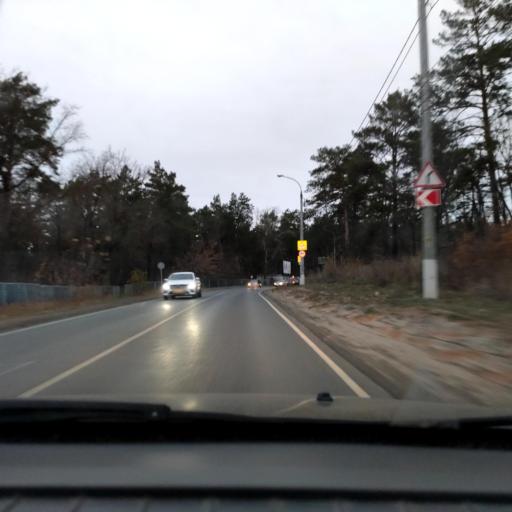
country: RU
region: Samara
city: Tol'yatti
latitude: 53.4862
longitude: 49.3129
